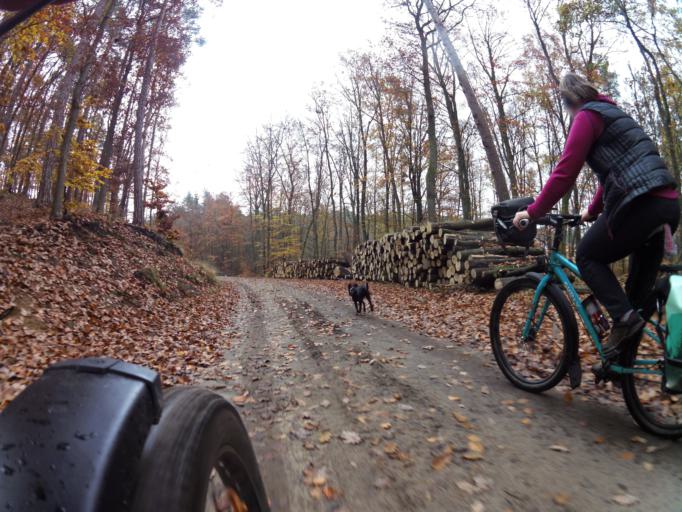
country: PL
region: Pomeranian Voivodeship
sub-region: Powiat pucki
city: Krokowa
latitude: 54.7470
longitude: 18.0925
